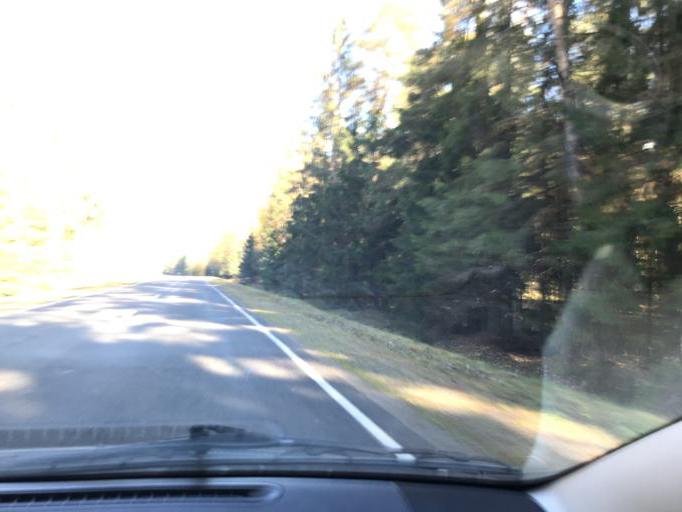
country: BY
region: Vitebsk
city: Lyepyel'
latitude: 54.9686
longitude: 28.7452
